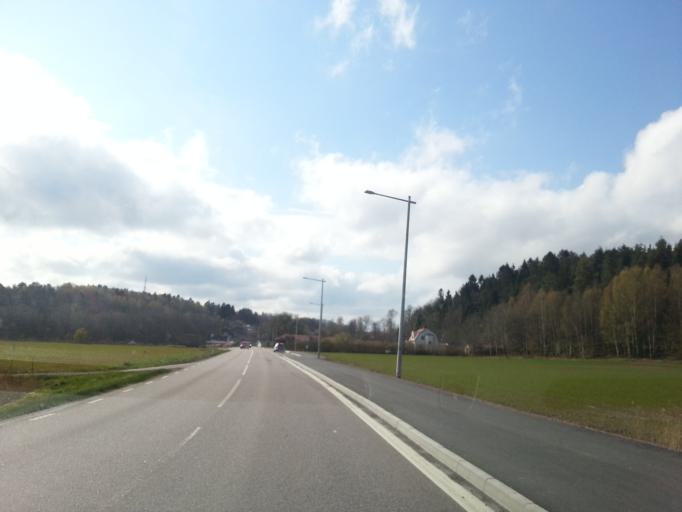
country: SE
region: Vaestra Goetaland
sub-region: Ale Kommun
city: Surte
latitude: 57.8101
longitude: 11.9968
